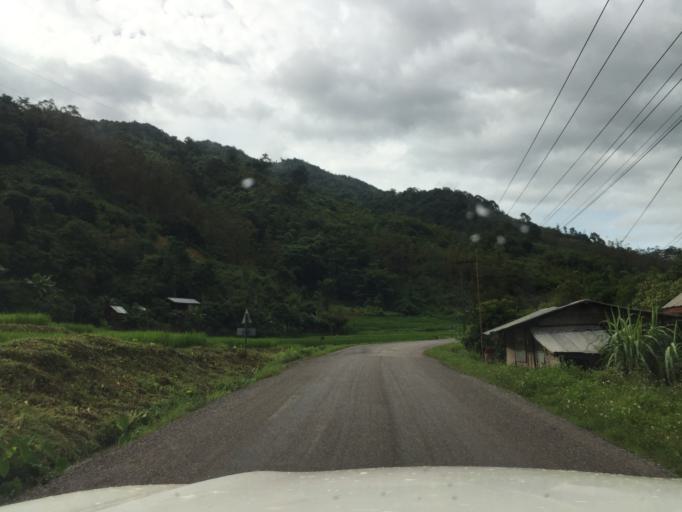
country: LA
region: Oudomxai
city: Muang La
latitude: 20.8135
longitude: 102.0914
